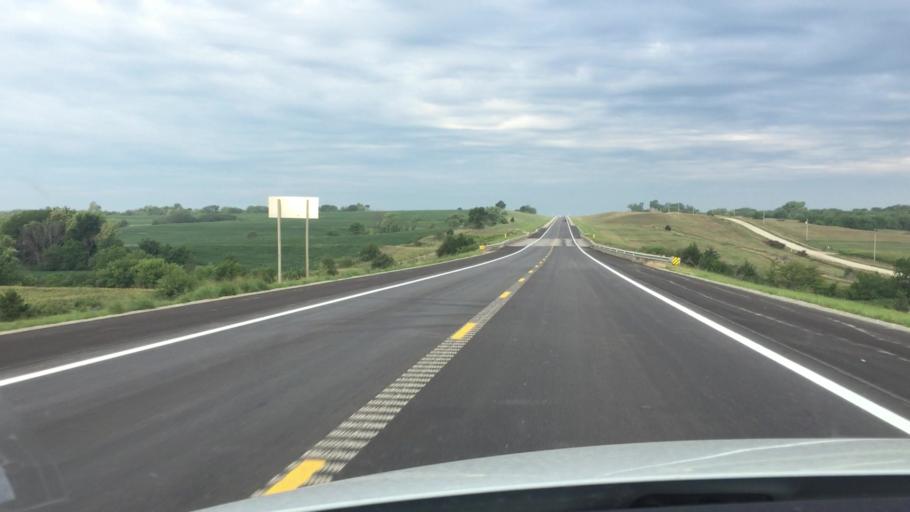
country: US
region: Kansas
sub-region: Doniphan County
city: Highland
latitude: 39.8412
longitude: -95.3760
